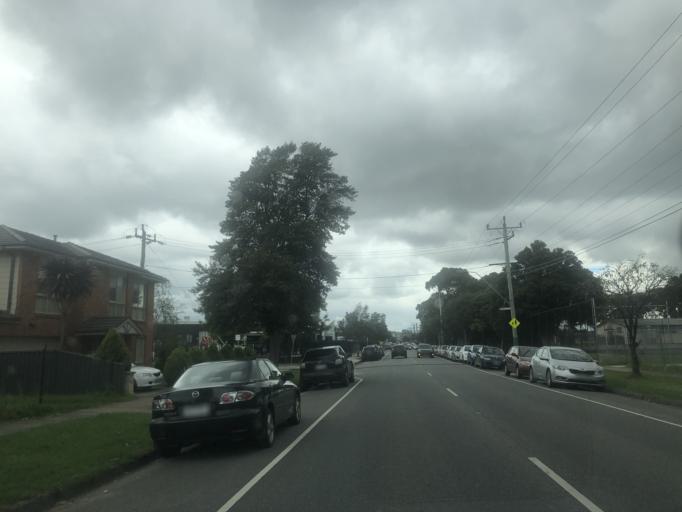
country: AU
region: Victoria
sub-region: Greater Dandenong
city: Dandenong North
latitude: -37.9764
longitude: 145.2114
